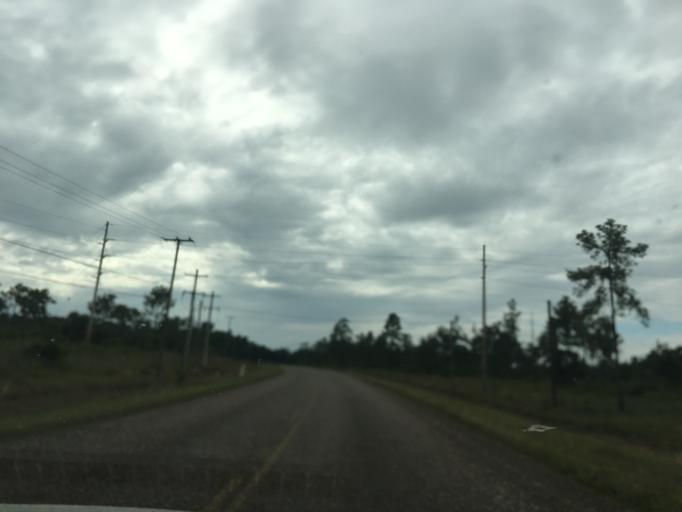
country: BZ
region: Stann Creek
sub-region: Dangriga
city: Dangriga
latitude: 16.7680
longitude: -88.3838
